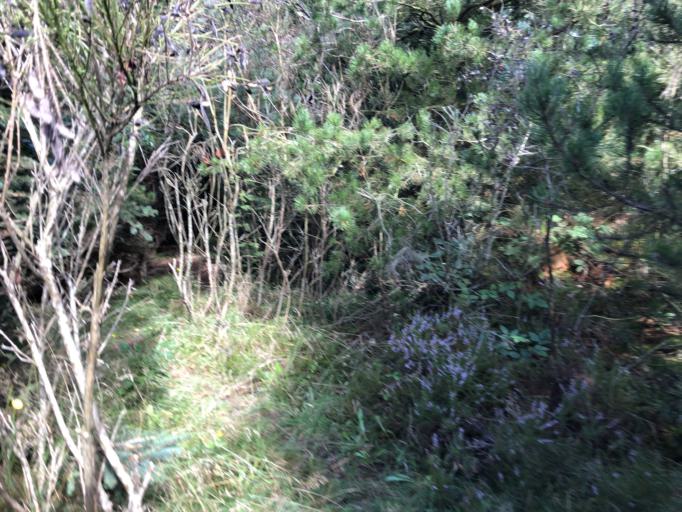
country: DK
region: Central Jutland
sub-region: Holstebro Kommune
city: Ulfborg
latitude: 56.3868
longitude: 8.3637
